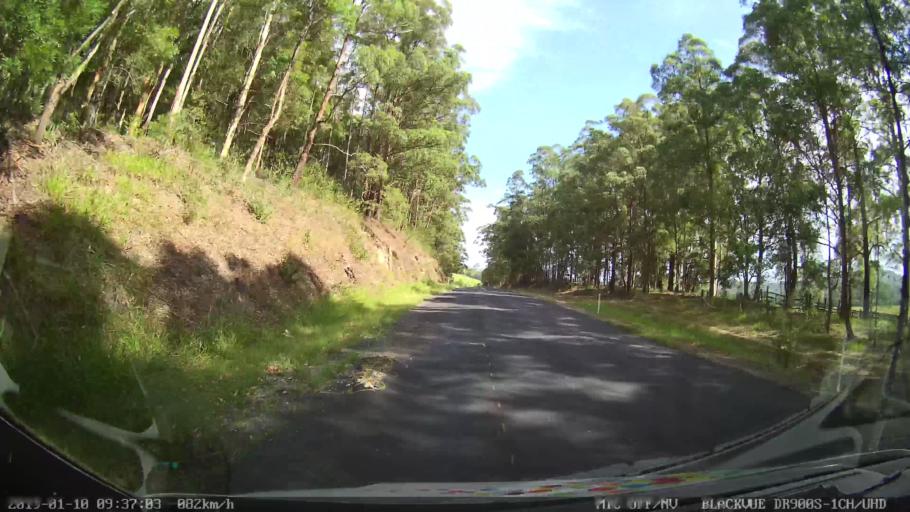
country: AU
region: New South Wales
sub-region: Coffs Harbour
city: Nana Glen
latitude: -30.1920
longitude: 153.0122
